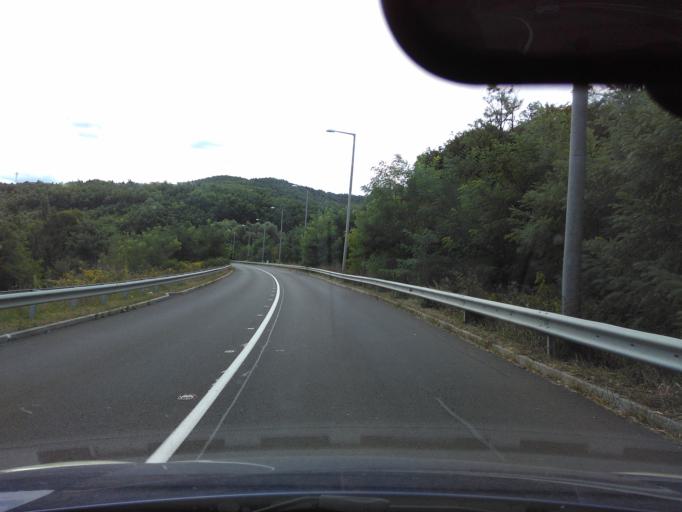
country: HU
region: Nograd
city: Salgotarjan
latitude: 48.1245
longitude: 19.8033
